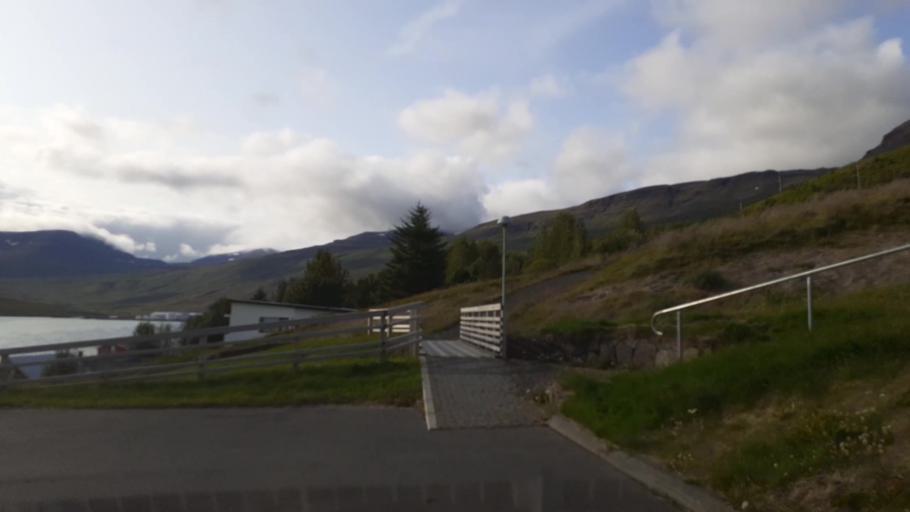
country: IS
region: East
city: Eskifjoerdur
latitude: 65.0662
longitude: -14.0014
